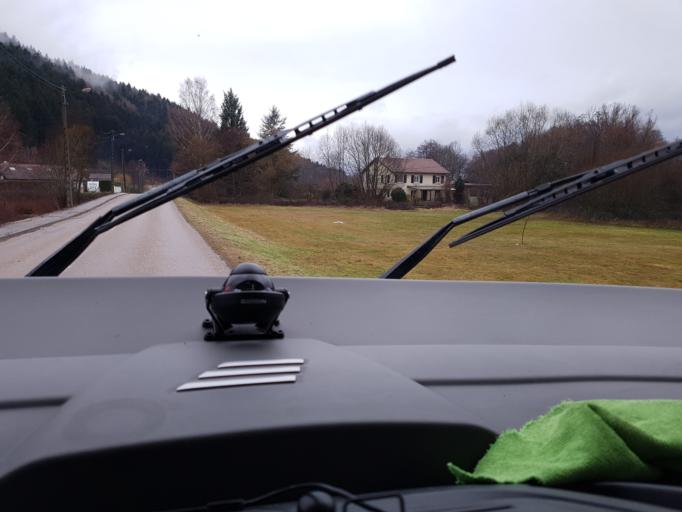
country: FR
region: Lorraine
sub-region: Departement des Vosges
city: Saint-Die-des-Vosges
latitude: 48.2921
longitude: 6.9214
